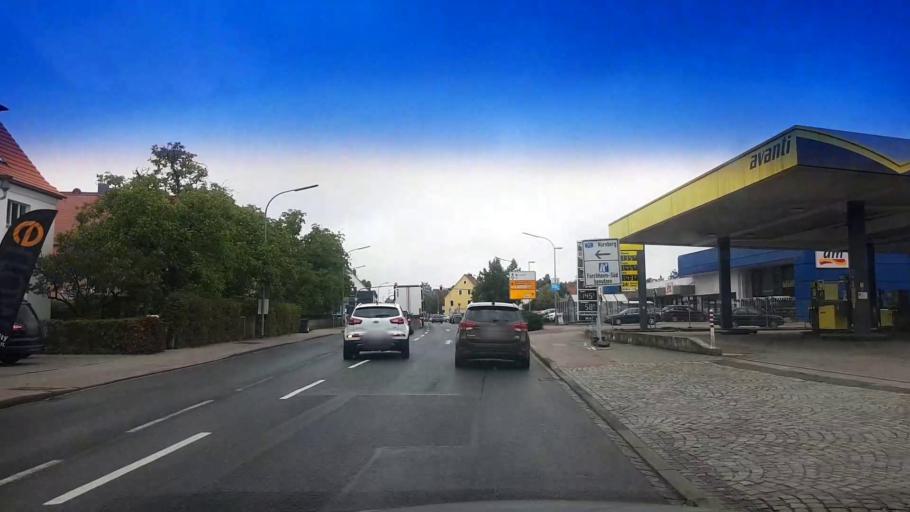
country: DE
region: Bavaria
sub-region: Upper Franconia
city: Forchheim
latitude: 49.7267
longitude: 11.0578
